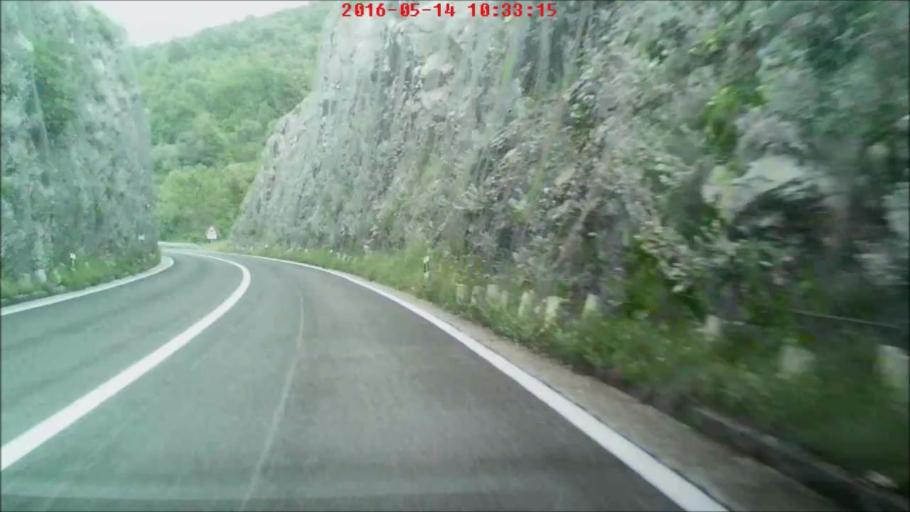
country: HR
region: Dubrovacko-Neretvanska
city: Podgora
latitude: 42.7722
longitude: 17.8853
